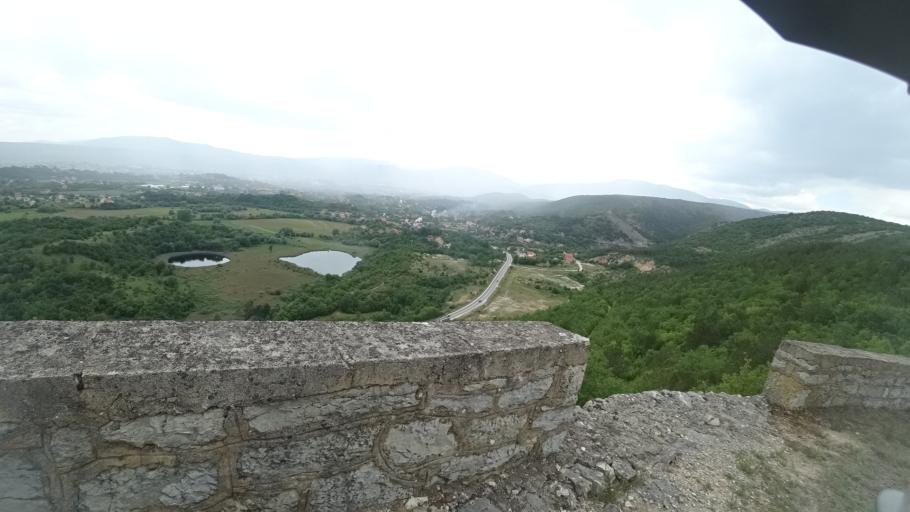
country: HR
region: Sibensko-Kniniska
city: Knin
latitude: 44.0327
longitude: 16.2284
